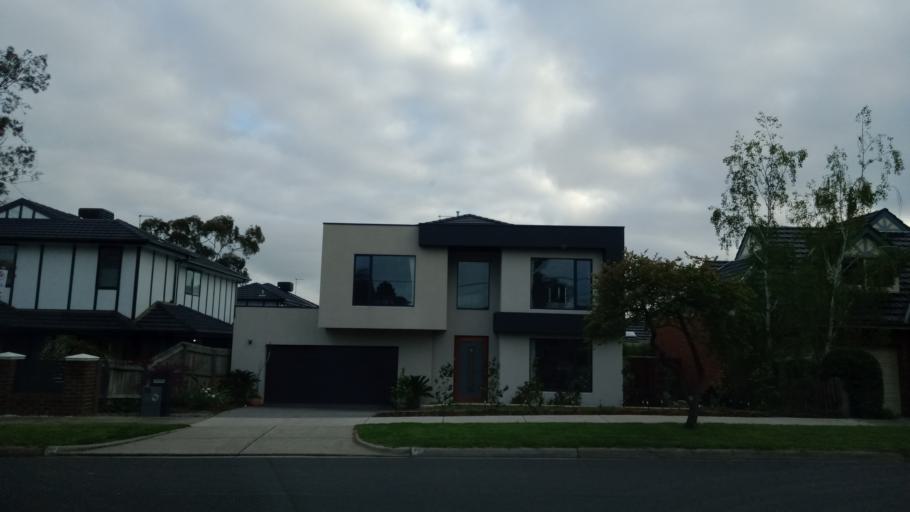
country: AU
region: Victoria
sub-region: Whitehorse
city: Burwood
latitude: -37.8733
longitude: 145.1317
